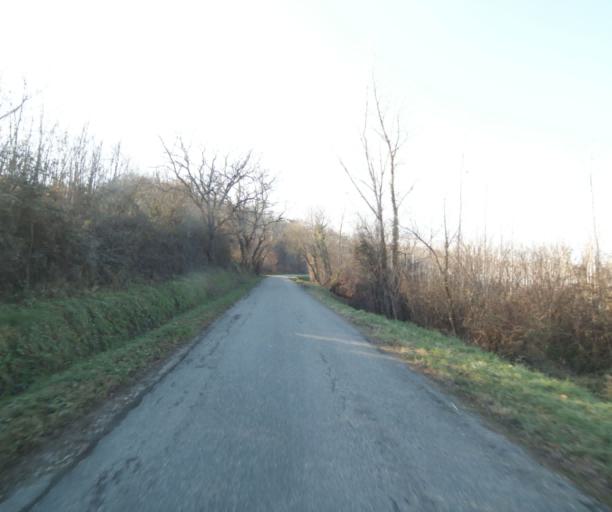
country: FR
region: Midi-Pyrenees
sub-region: Departement du Tarn-et-Garonne
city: Moissac
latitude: 44.1256
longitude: 1.0970
